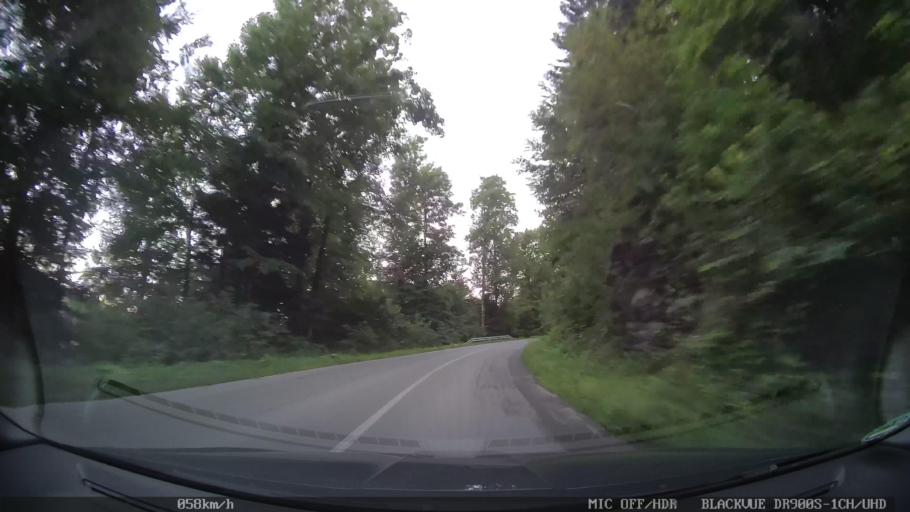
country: HR
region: Primorsko-Goranska
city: Vrbovsko
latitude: 45.2002
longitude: 15.0265
